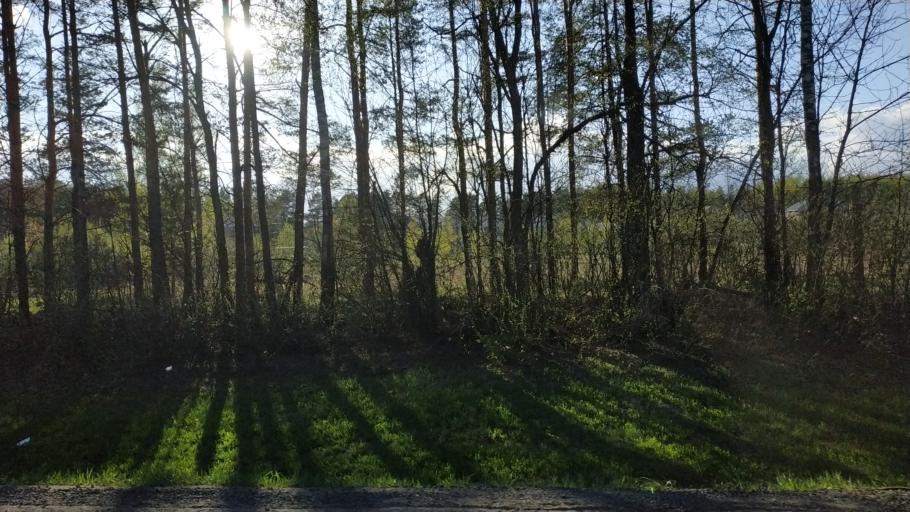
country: RU
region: Moskovskaya
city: Gzhel'
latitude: 55.6416
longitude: 38.3686
